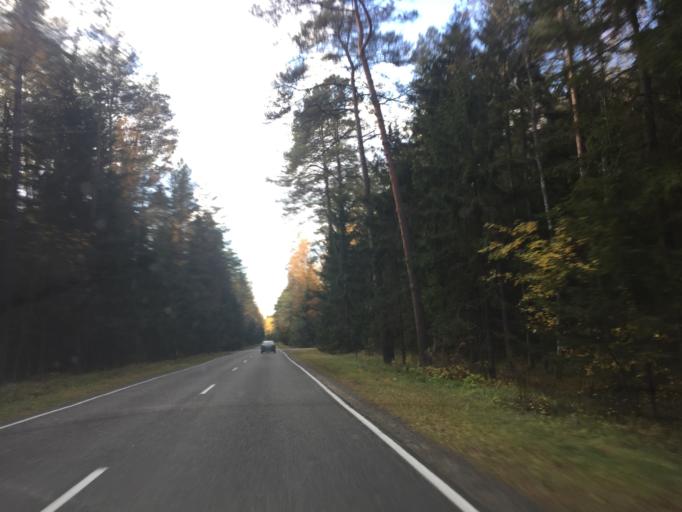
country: BY
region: Minsk
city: Narach
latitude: 54.9423
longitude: 26.5730
